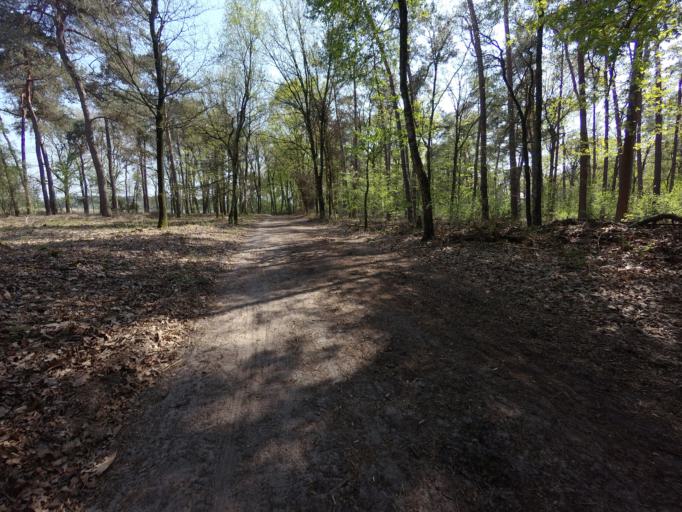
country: NL
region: North Brabant
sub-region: Gemeente Goirle
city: Goirle
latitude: 51.5002
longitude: 5.0113
